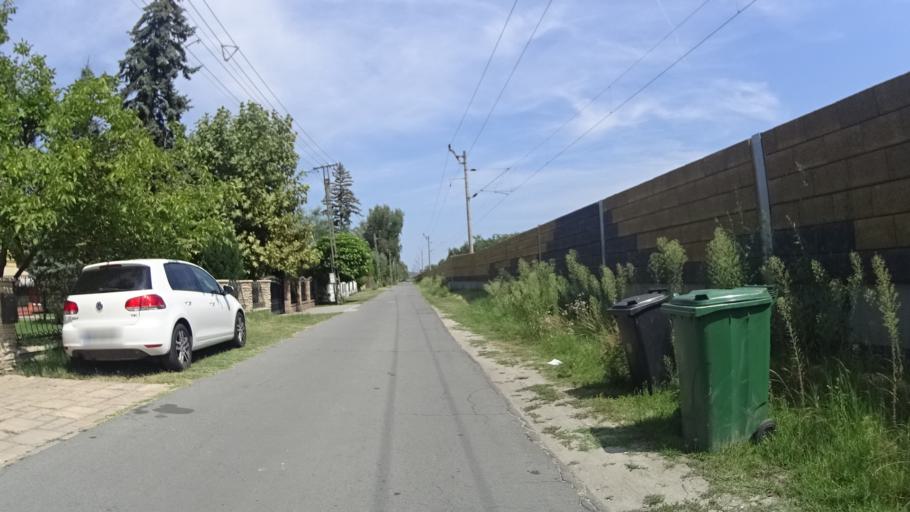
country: HU
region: Somogy
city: Fonyod
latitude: 46.7610
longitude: 17.5981
